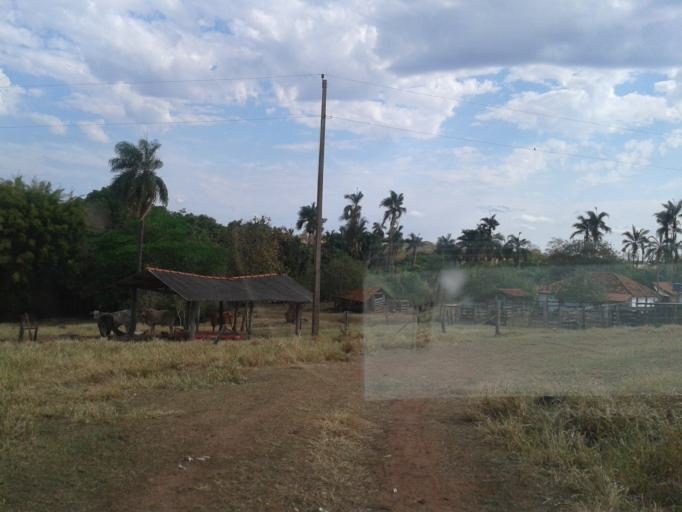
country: BR
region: Minas Gerais
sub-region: Ituiutaba
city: Ituiutaba
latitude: -19.0269
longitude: -49.2109
